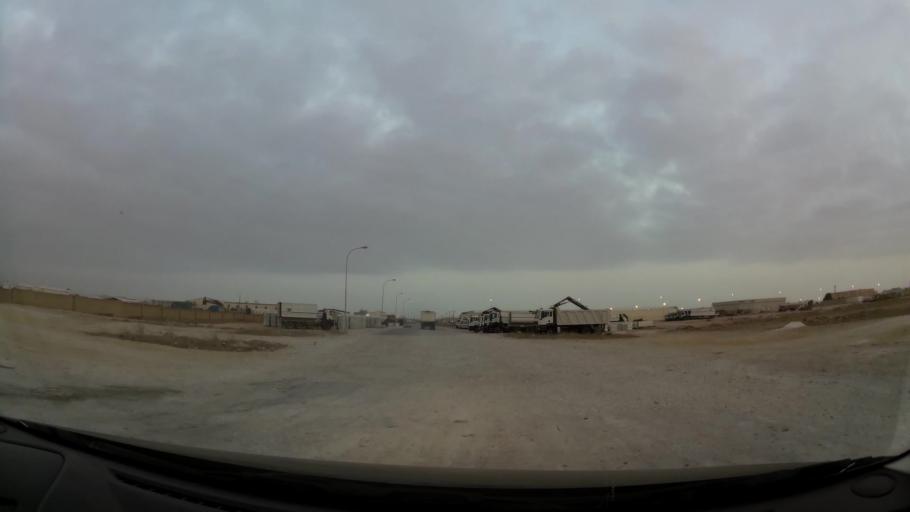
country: OM
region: Zufar
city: Salalah
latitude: 17.0371
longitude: 54.0419
